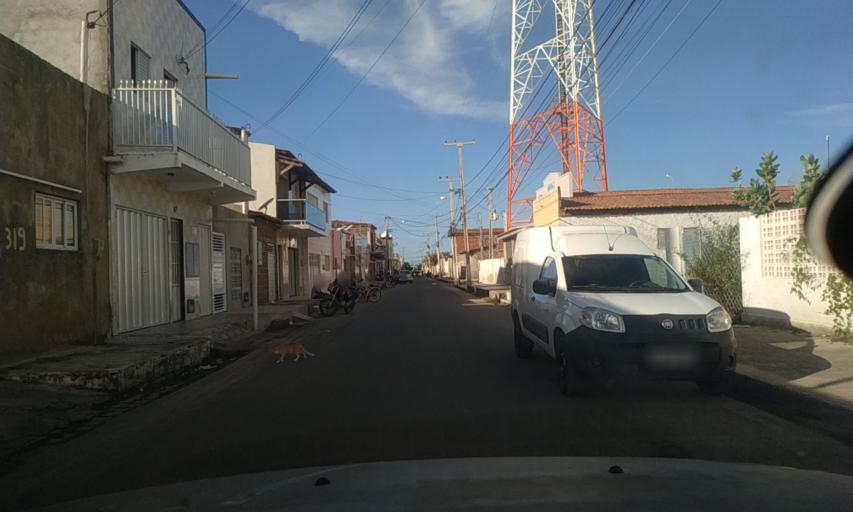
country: BR
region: Rio Grande do Norte
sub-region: Areia Branca
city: Areia Branca
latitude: -4.9530
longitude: -37.1268
